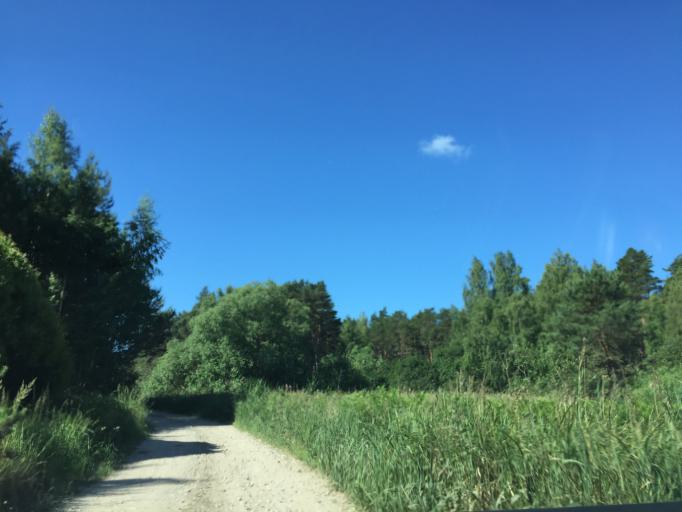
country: LV
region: Ventspils
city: Ventspils
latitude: 57.4563
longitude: 21.6328
